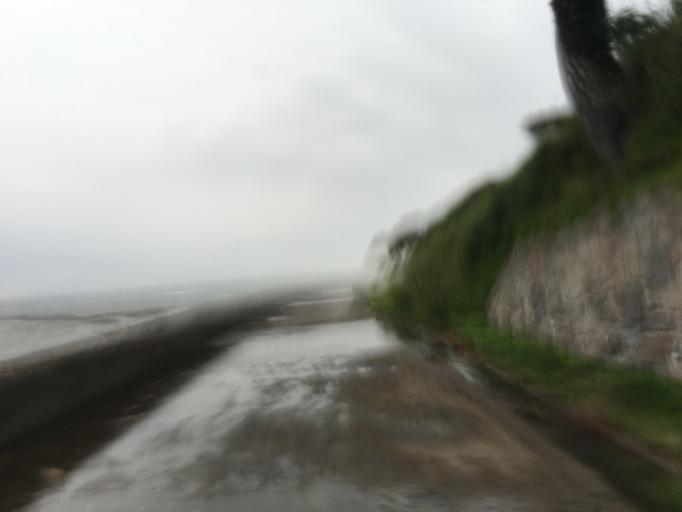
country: JP
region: Aichi
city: Ishiki
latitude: 34.7310
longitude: 137.0363
